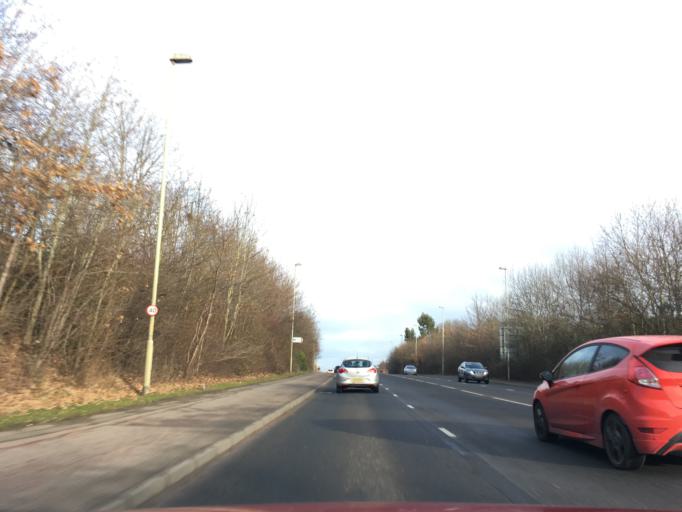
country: GB
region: England
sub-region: Gloucestershire
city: Gloucester
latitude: 51.8476
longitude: -2.2646
